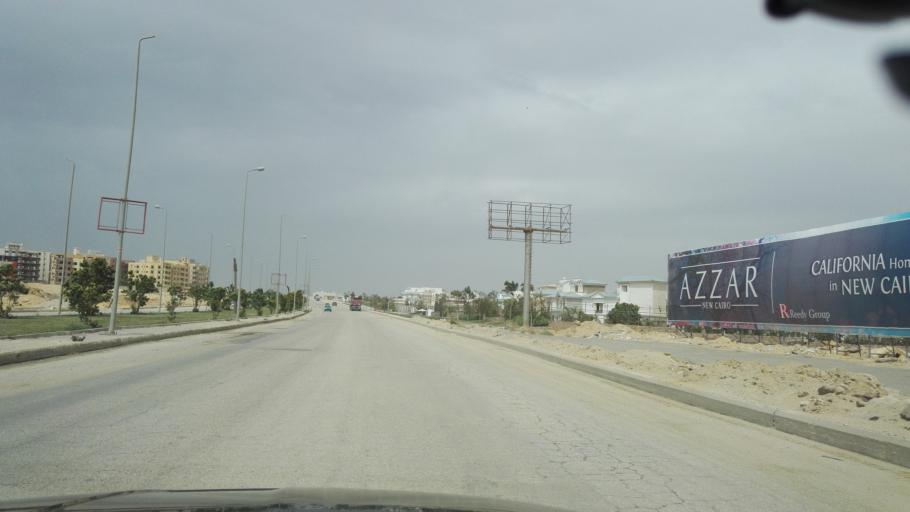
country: EG
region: Muhafazat al Qalyubiyah
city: Al Khankah
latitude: 30.0299
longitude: 31.5291
